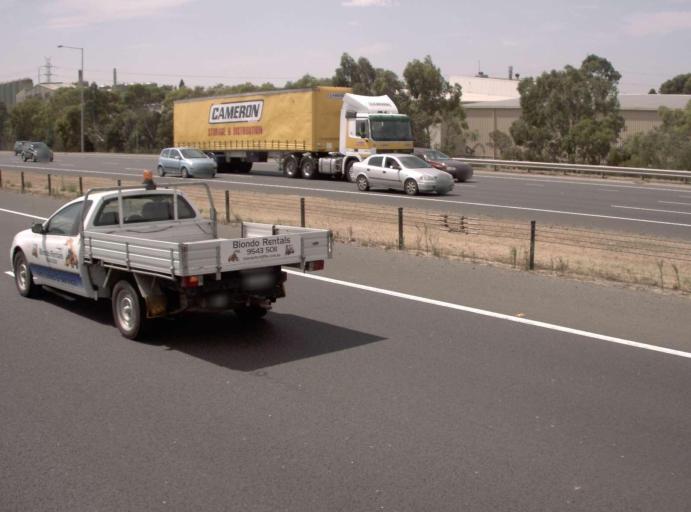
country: AU
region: Victoria
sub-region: Brimbank
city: Sunshine West
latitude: -37.8206
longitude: 144.8098
